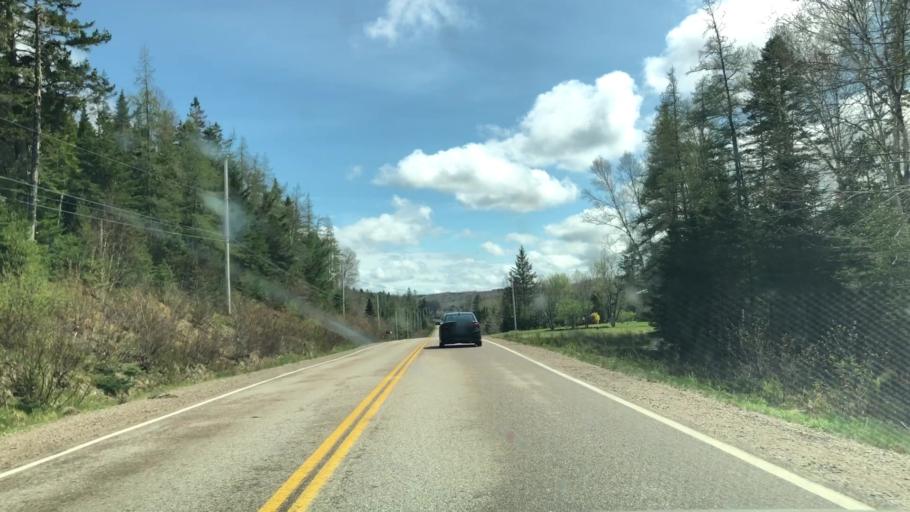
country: CA
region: Nova Scotia
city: Antigonish
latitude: 45.2078
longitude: -62.0038
